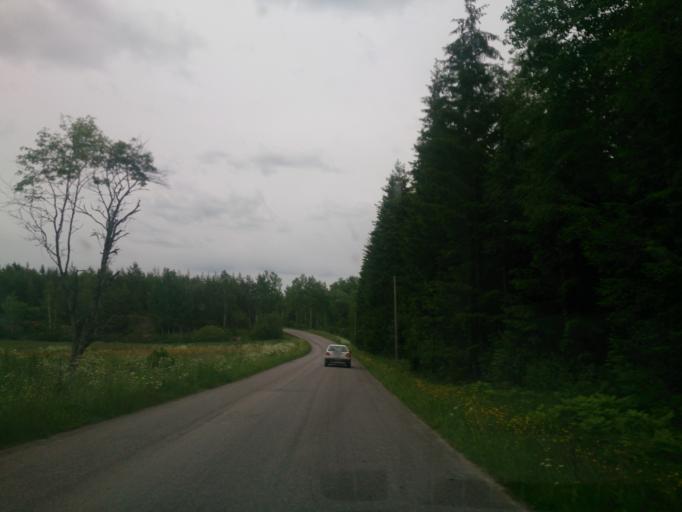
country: SE
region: OEstergoetland
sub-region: Valdemarsviks Kommun
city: Gusum
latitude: 58.3185
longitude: 16.3761
